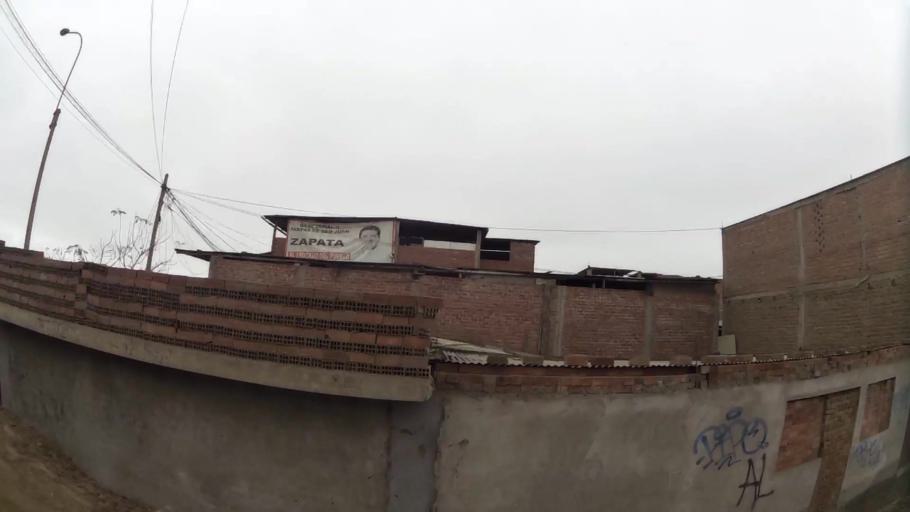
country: PE
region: Lima
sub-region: Lima
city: Surco
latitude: -12.1754
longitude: -76.9563
